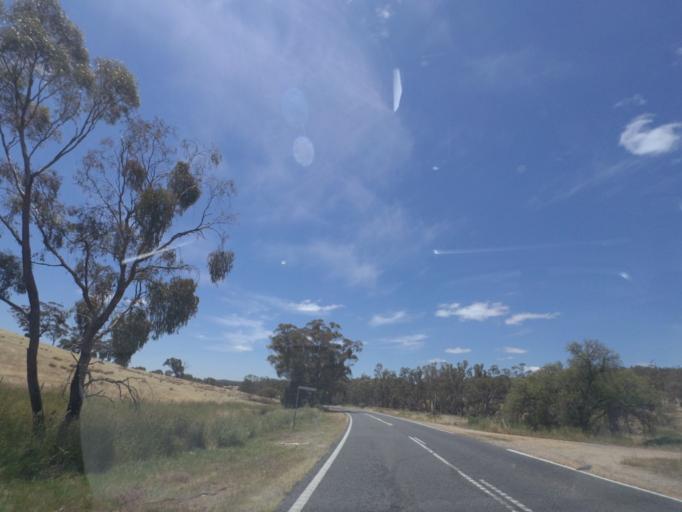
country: AU
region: Victoria
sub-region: Mount Alexander
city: Castlemaine
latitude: -37.2007
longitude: 144.1448
